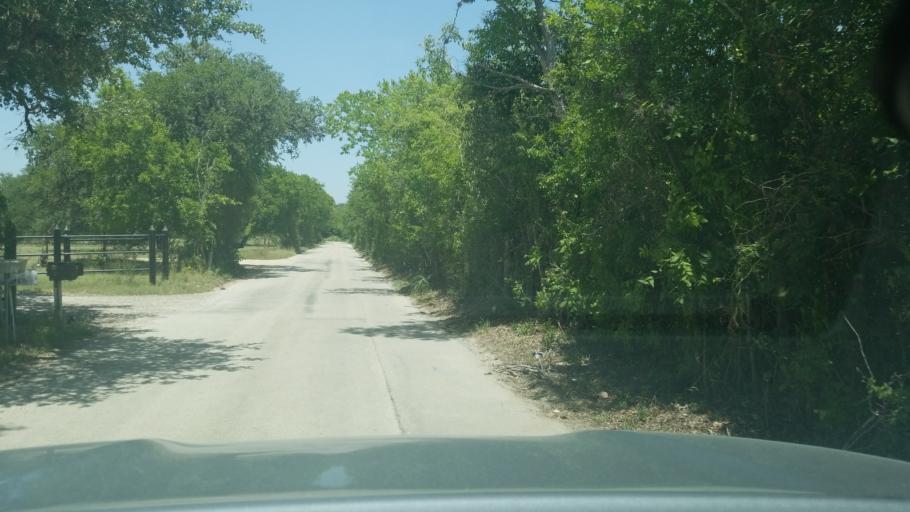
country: US
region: Texas
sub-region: Guadalupe County
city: Northcliff
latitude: 29.5919
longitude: -98.2266
